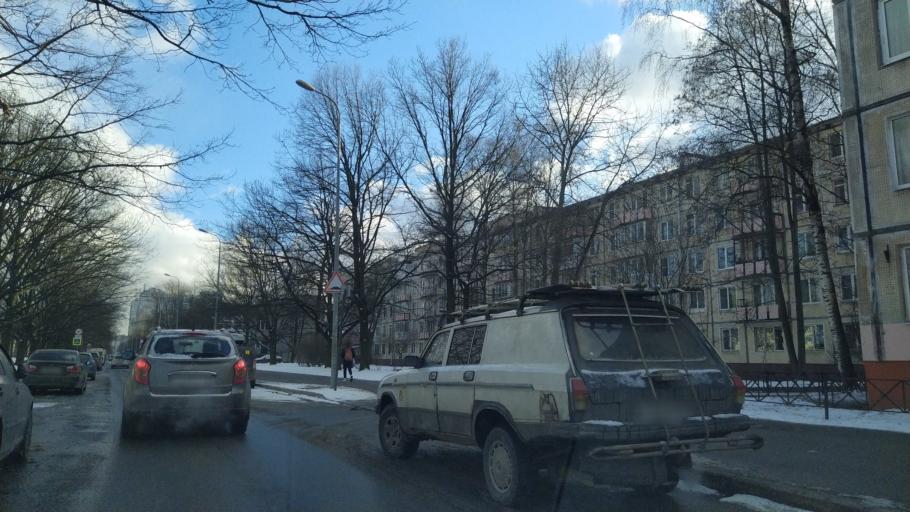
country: RU
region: St.-Petersburg
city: Kupchino
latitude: 59.8635
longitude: 30.3473
